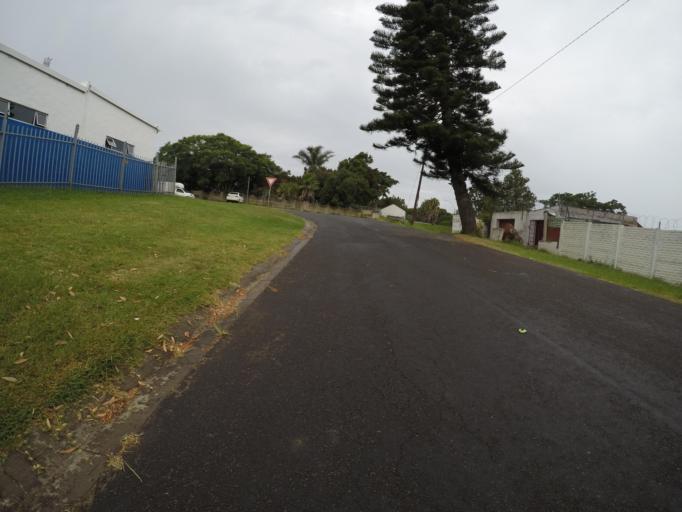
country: ZA
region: Eastern Cape
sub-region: Buffalo City Metropolitan Municipality
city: East London
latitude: -32.9879
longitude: 27.8566
